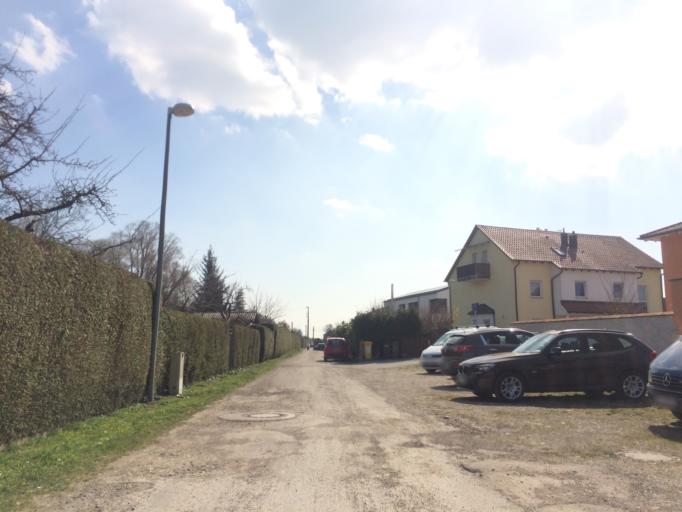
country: DE
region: Bavaria
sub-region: Swabia
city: Gersthofen
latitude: 48.4032
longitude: 10.8871
